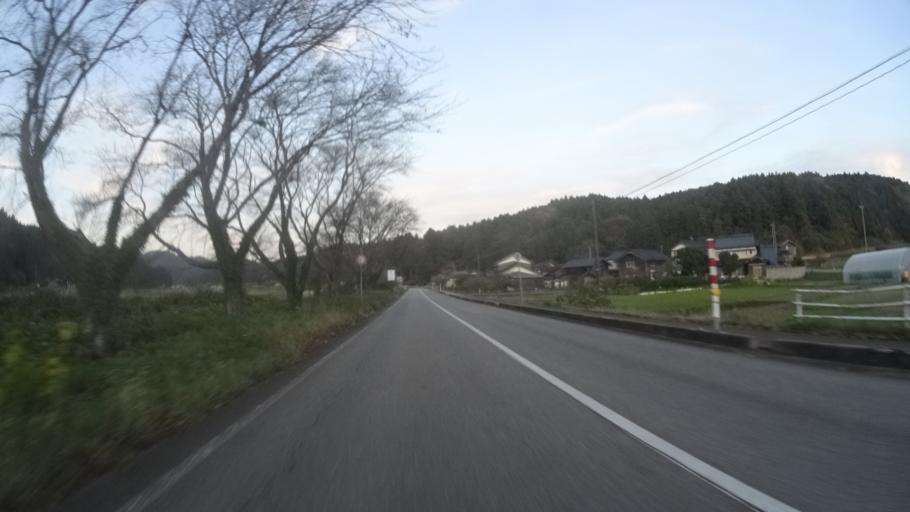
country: JP
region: Ishikawa
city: Nanao
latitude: 37.2970
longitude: 136.7945
